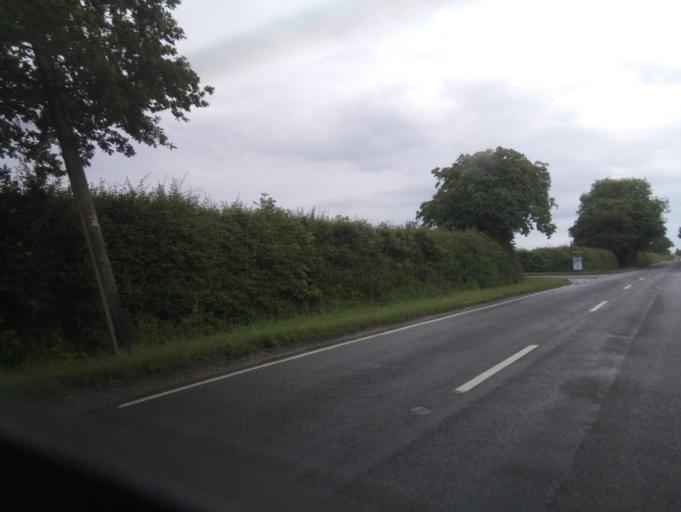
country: GB
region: England
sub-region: Lincolnshire
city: Great Gonerby
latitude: 53.0010
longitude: -0.6681
